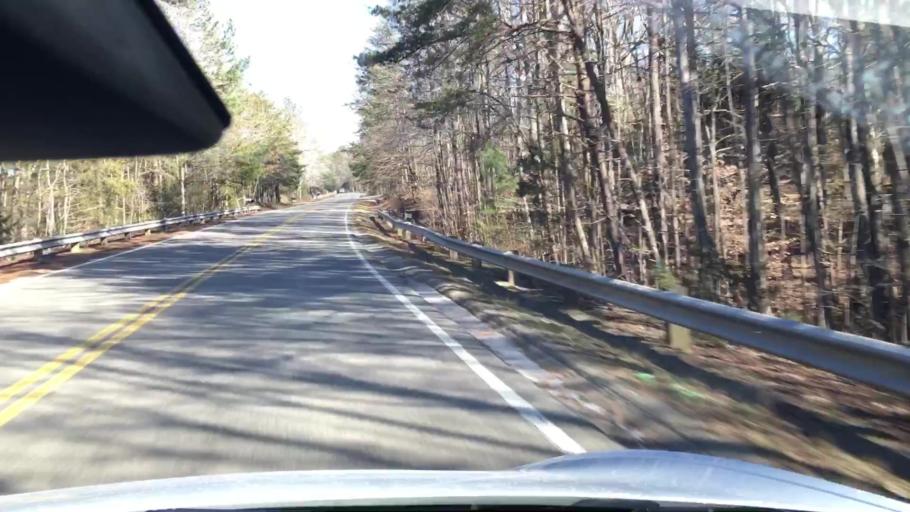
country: US
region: Virginia
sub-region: Powhatan County
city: Powhatan
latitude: 37.5322
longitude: -77.8004
